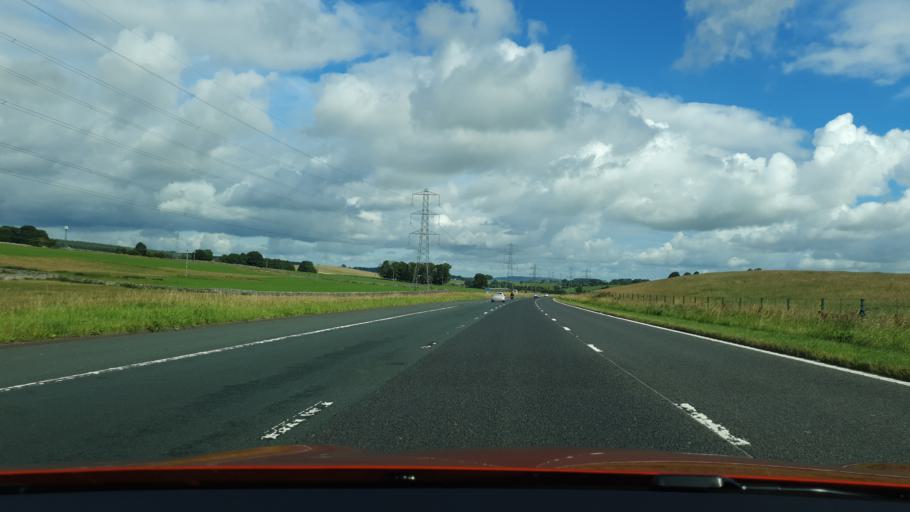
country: GB
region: England
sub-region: Cumbria
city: Penrith
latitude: 54.5495
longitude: -2.6711
